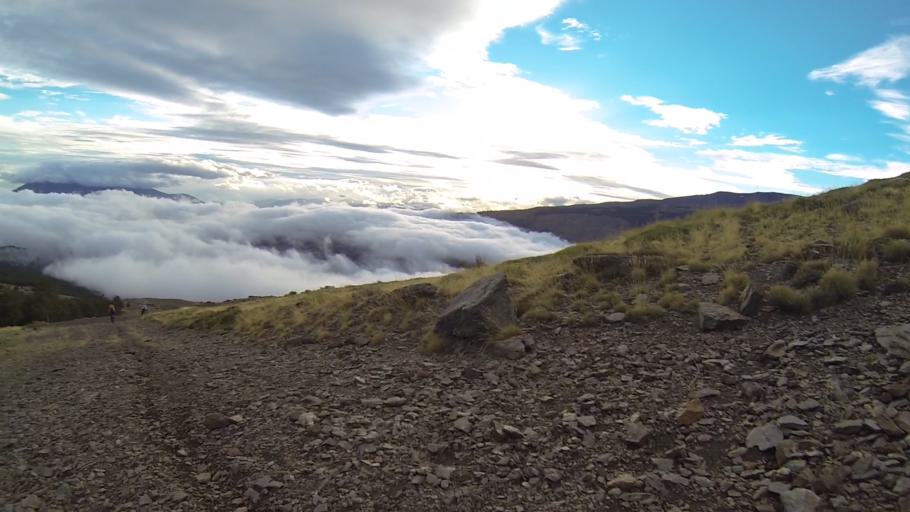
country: ES
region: Andalusia
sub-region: Provincia de Granada
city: Capileira
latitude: 36.9702
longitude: -3.3362
